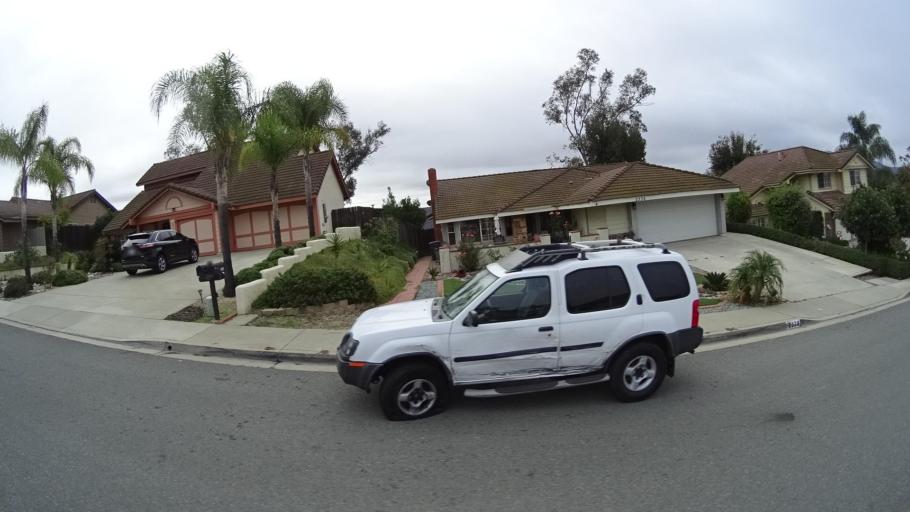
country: US
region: California
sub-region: San Diego County
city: Rancho San Diego
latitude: 32.7517
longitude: -116.9122
